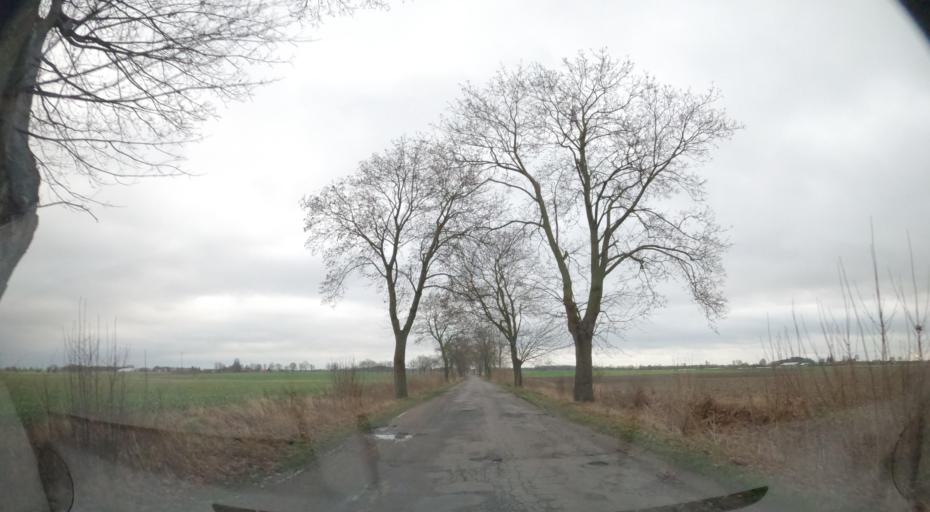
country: PL
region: Greater Poland Voivodeship
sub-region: Powiat pilski
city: Wysoka
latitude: 53.2677
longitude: 17.1086
